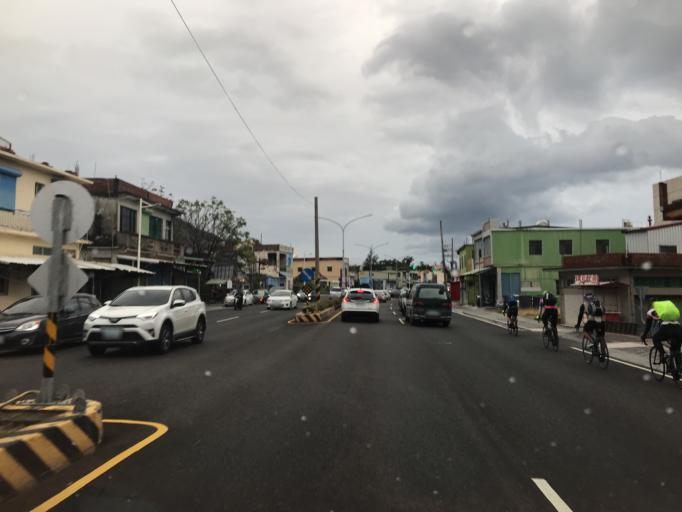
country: TW
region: Taiwan
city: Hengchun
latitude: 22.1904
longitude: 120.6917
